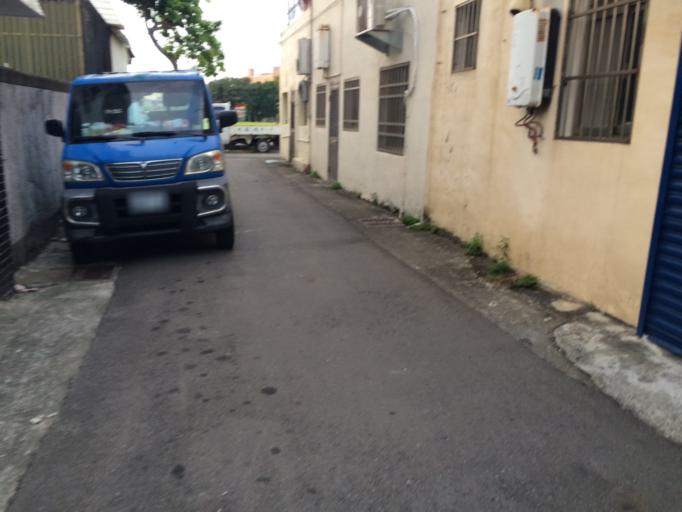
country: TW
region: Taiwan
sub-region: Hsinchu
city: Hsinchu
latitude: 24.7977
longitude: 120.9595
